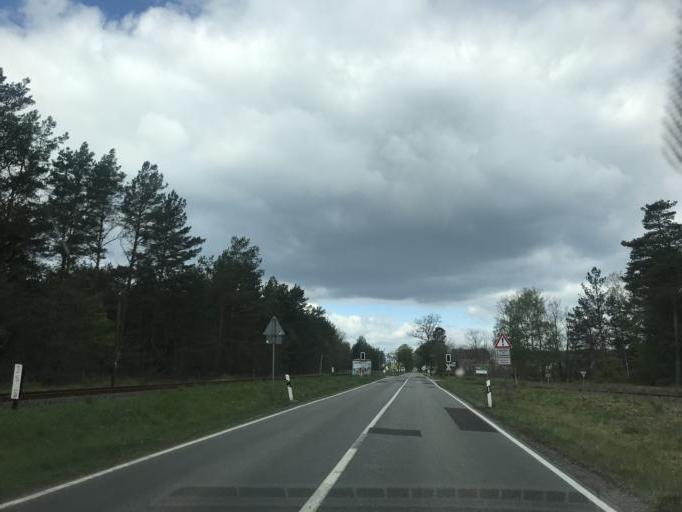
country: DE
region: Brandenburg
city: Rheinsberg
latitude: 53.0856
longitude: 12.9116
